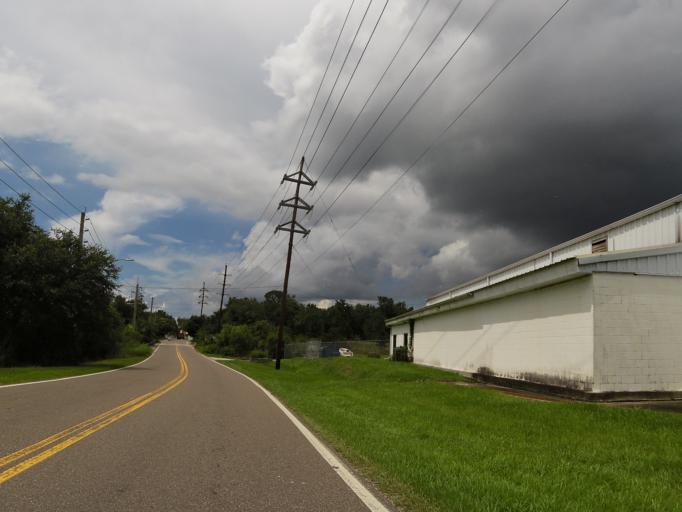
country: US
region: Florida
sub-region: Duval County
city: Jacksonville
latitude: 30.3703
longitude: -81.6392
